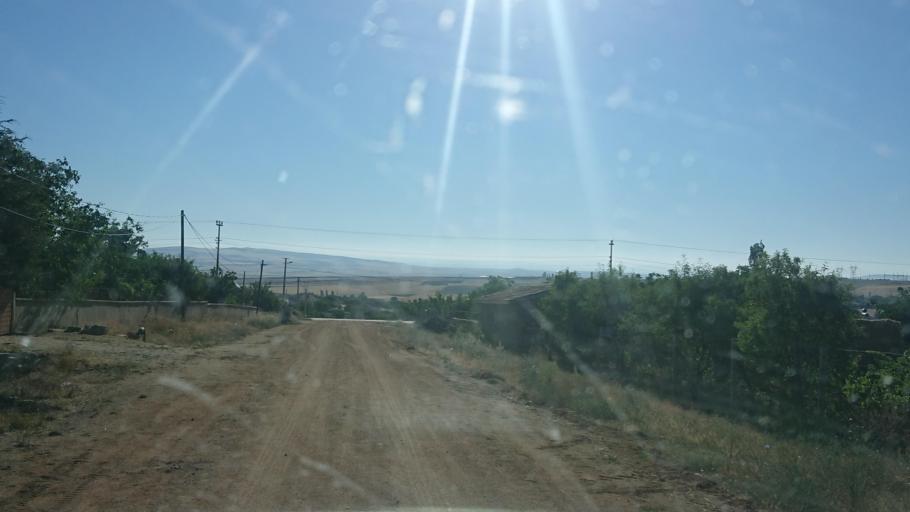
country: TR
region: Aksaray
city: Agacoren
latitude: 38.8751
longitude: 33.9512
